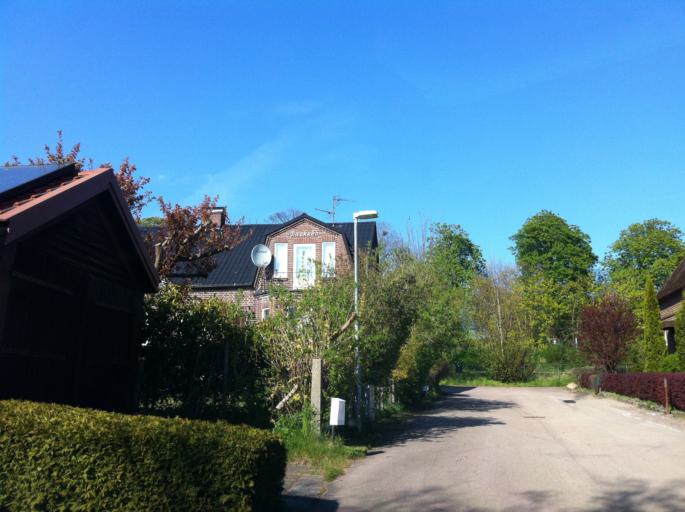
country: SE
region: Skane
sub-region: Svalovs Kommun
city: Kagerod
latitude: 55.9668
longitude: 13.0496
